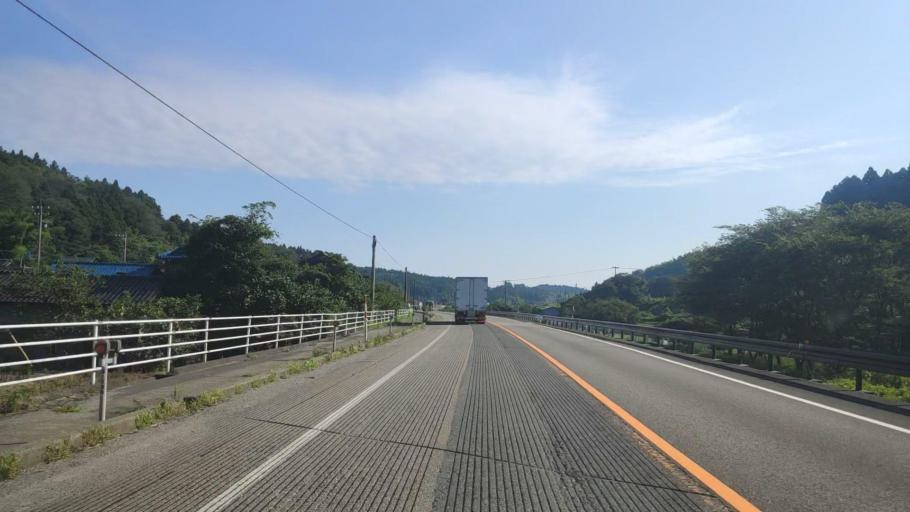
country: JP
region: Fukui
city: Maruoka
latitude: 36.2815
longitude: 136.2930
